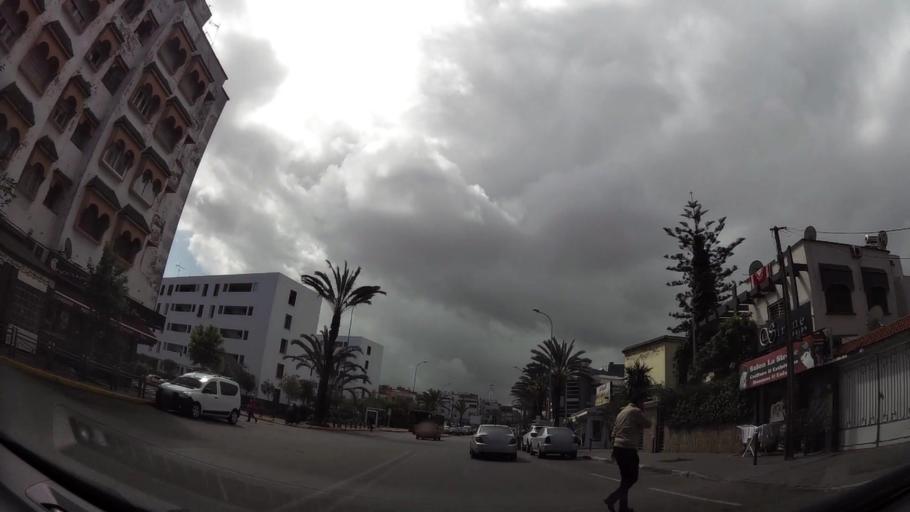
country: MA
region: Grand Casablanca
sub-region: Casablanca
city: Casablanca
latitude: 33.5497
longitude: -7.6024
